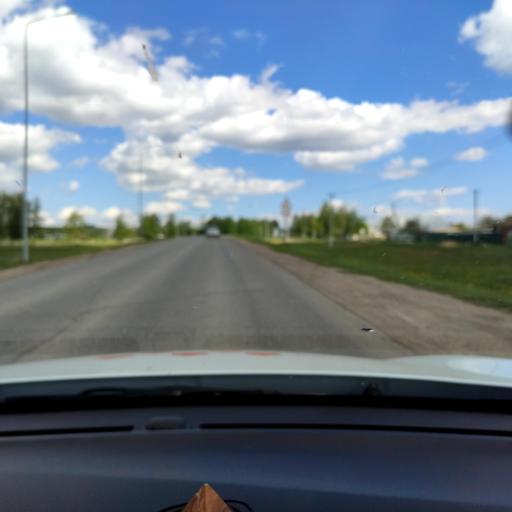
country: RU
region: Tatarstan
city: Kuybyshevskiy Zaton
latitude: 55.1871
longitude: 49.2436
